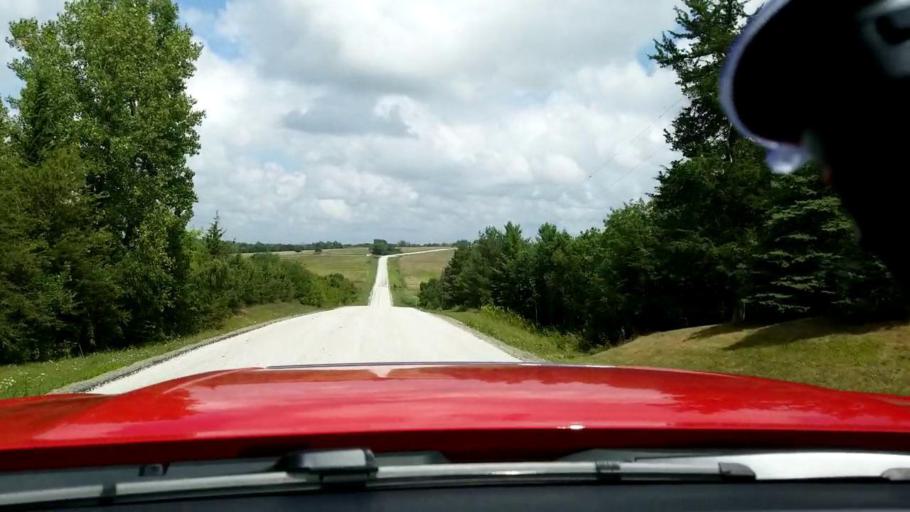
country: US
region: Iowa
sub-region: Decatur County
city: Lamoni
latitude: 40.6461
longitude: -94.0530
